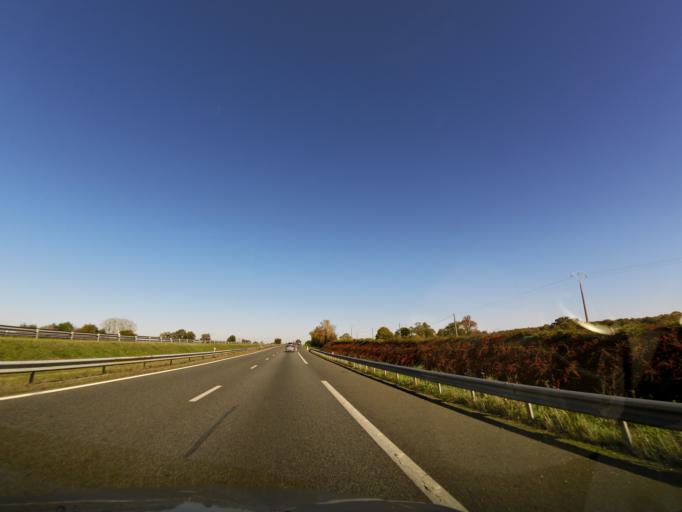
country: FR
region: Brittany
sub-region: Departement d'Ille-et-Vilaine
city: Pance
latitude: 47.9001
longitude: -1.6862
